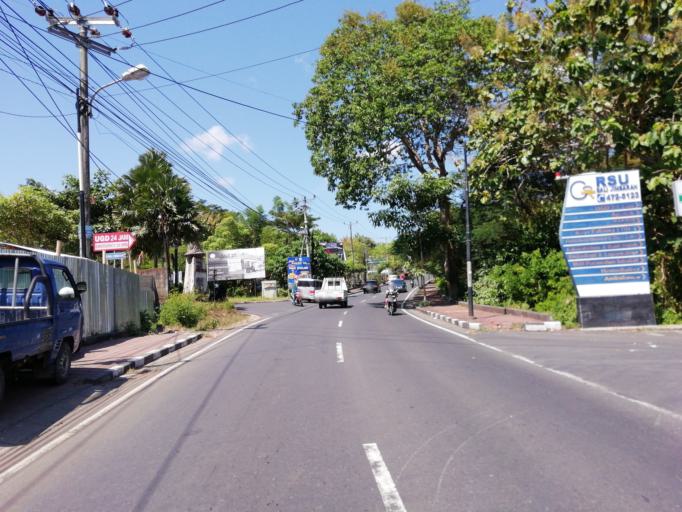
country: ID
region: Bali
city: Jimbaran
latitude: -8.7907
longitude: 115.1775
